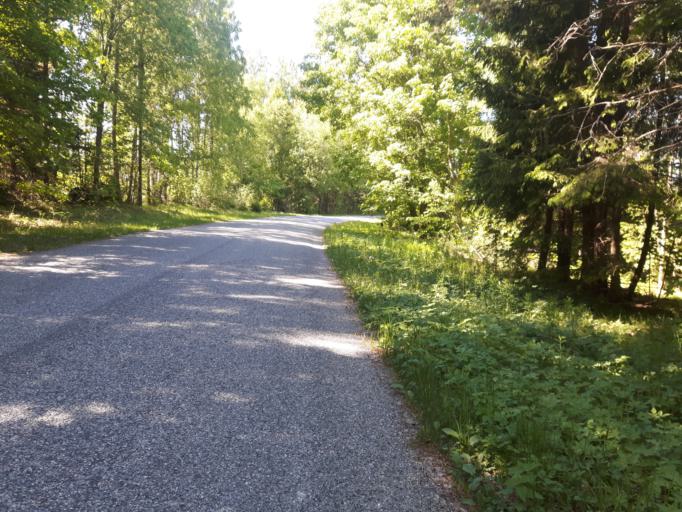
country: EE
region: Laeaene-Virumaa
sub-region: Haljala vald
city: Haljala
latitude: 59.5610
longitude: 26.3134
